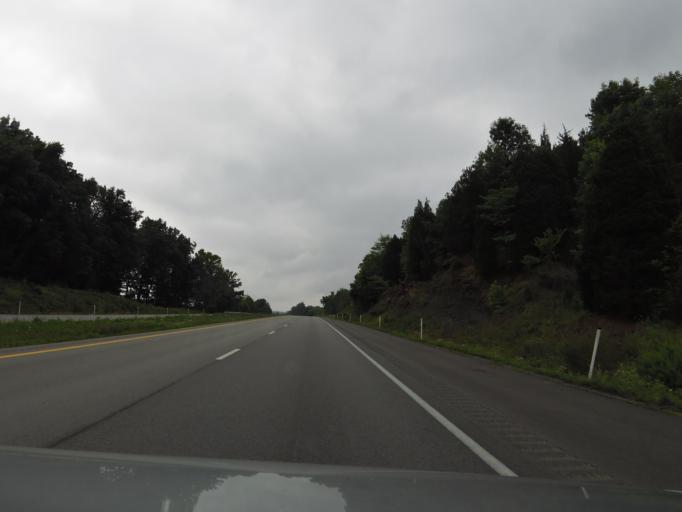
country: US
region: Kentucky
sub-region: Grayson County
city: Leitchfield
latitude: 37.4132
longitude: -86.4207
